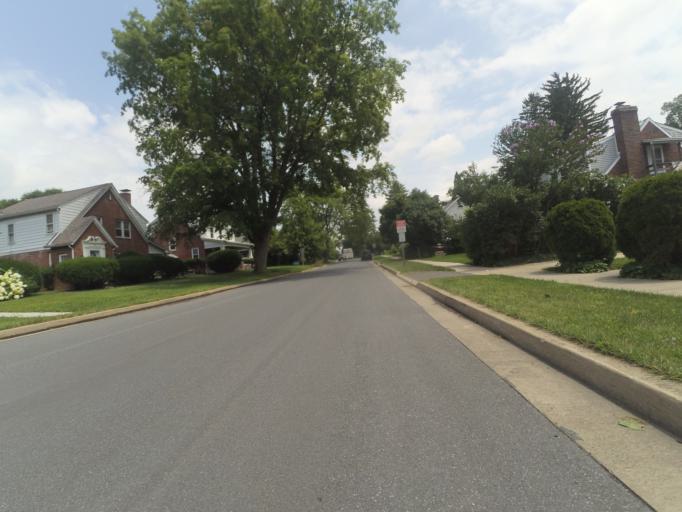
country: US
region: Pennsylvania
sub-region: Centre County
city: State College
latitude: 40.7846
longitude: -77.8718
